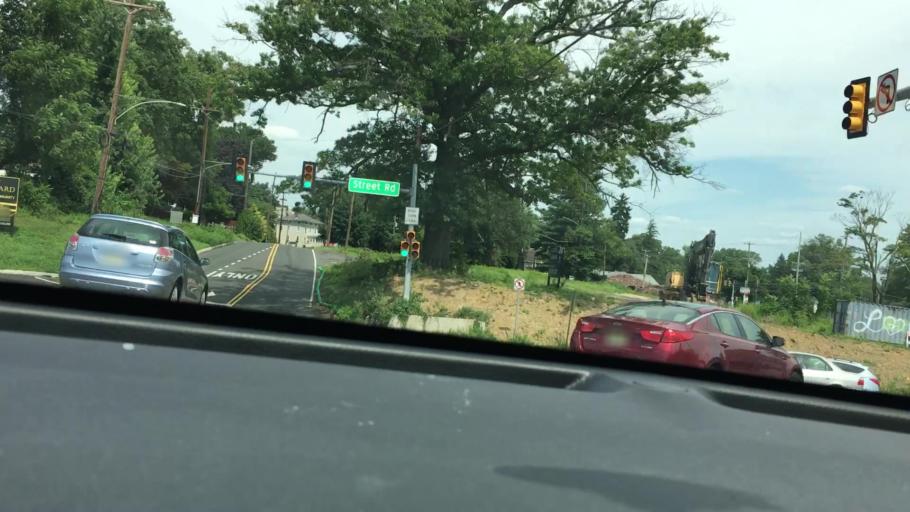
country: US
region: Pennsylvania
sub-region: Bucks County
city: Trevose
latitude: 40.1393
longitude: -74.9881
